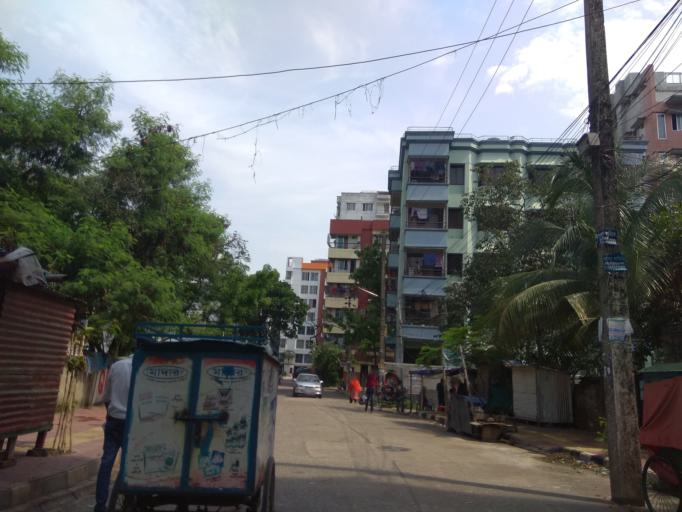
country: BD
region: Dhaka
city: Azimpur
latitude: 23.8085
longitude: 90.3557
